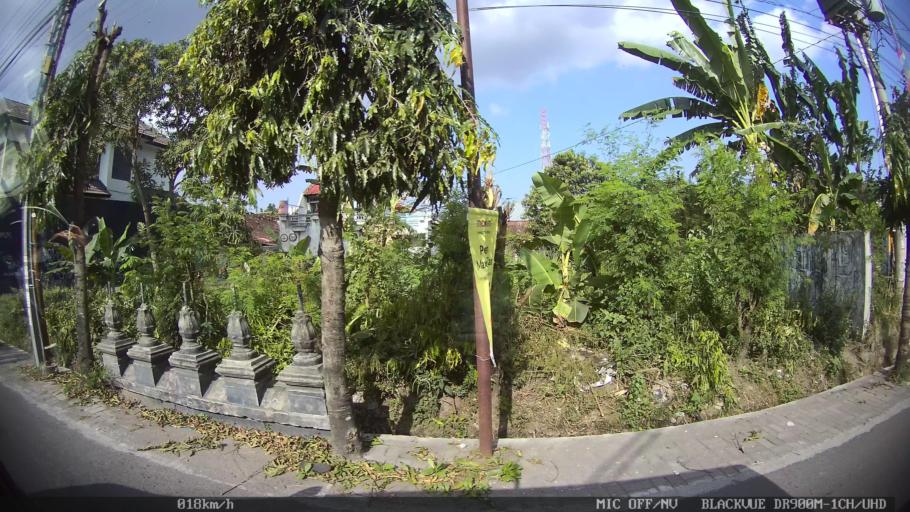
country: ID
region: Daerah Istimewa Yogyakarta
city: Gamping Lor
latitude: -7.7964
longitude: 110.3457
